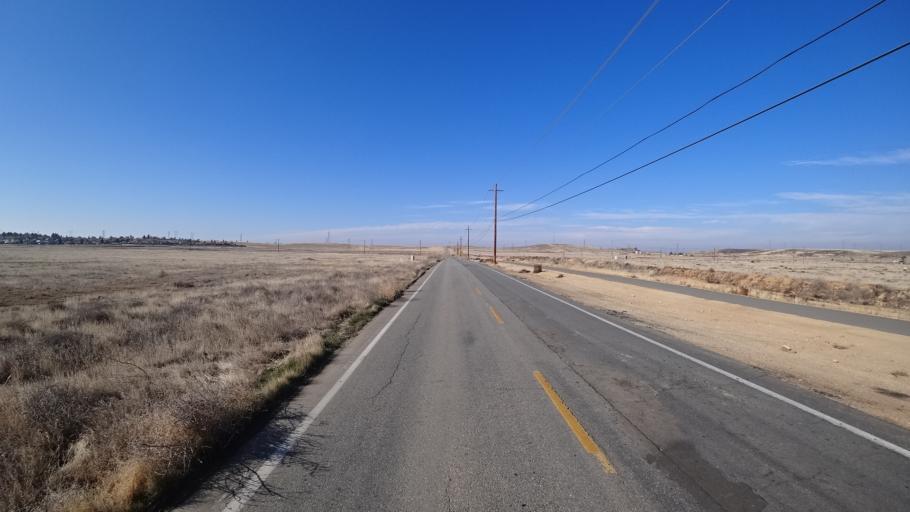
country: US
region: California
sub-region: Kern County
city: Oildale
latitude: 35.4125
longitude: -118.9105
